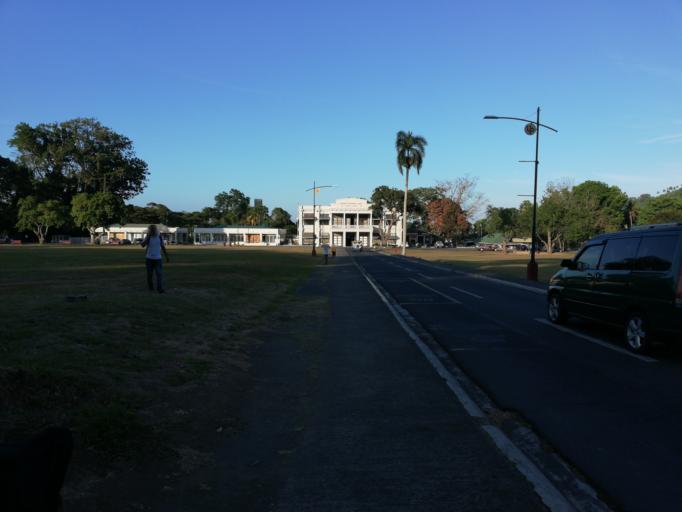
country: PH
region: Calabarzon
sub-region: Province of Laguna
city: Los Banos
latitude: 14.1610
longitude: 121.2414
